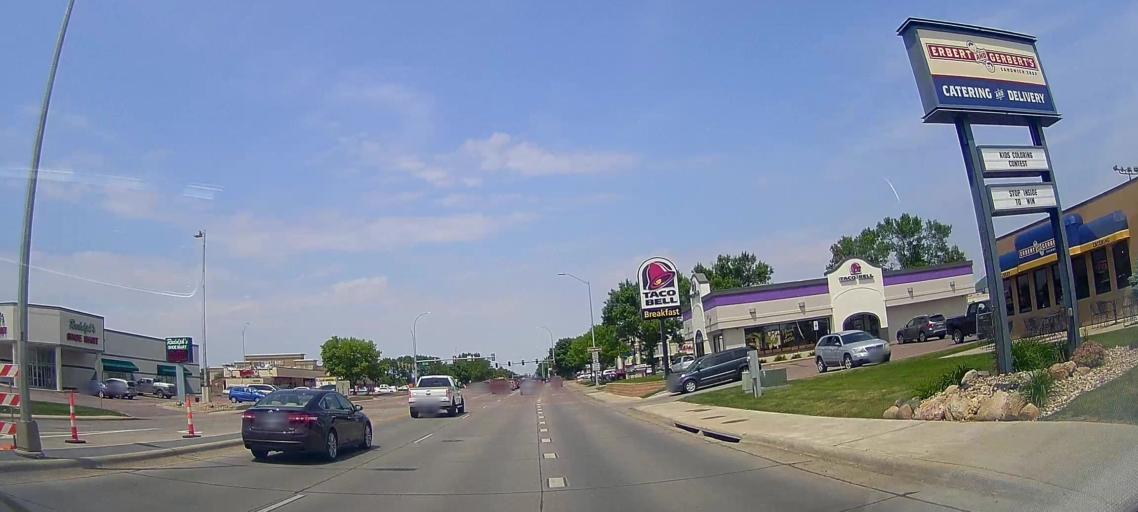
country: US
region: South Dakota
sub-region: Minnehaha County
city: Sioux Falls
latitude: 43.5136
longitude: -96.7709
